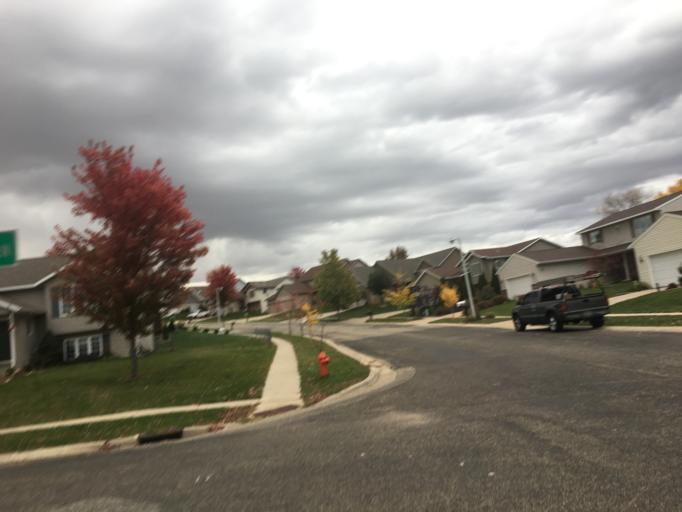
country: US
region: Minnesota
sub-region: Olmsted County
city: Oronoco
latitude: 44.0865
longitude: -92.5270
